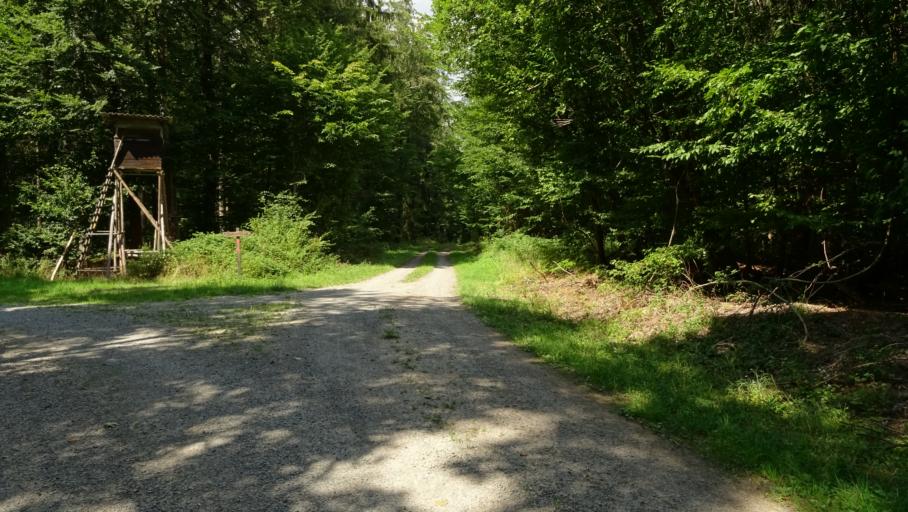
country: DE
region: Baden-Wuerttemberg
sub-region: Karlsruhe Region
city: Neckargerach
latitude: 49.4138
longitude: 9.1011
